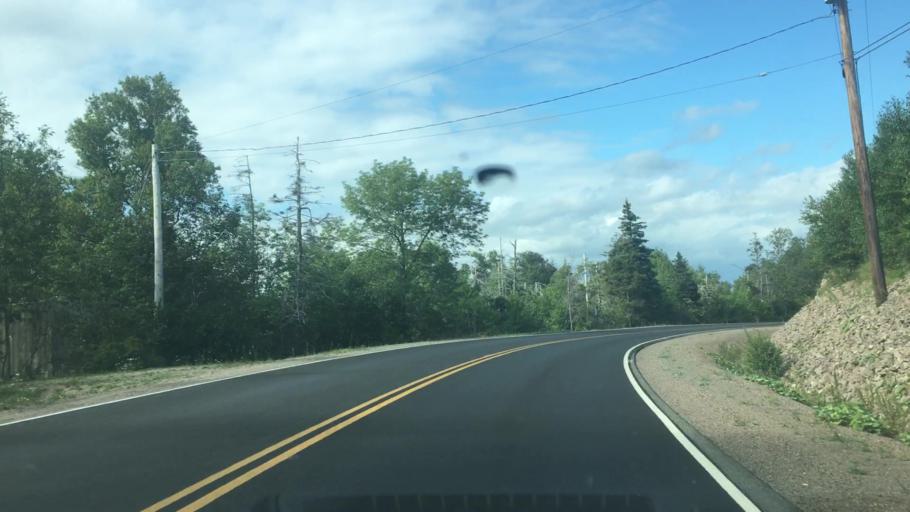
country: CA
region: Nova Scotia
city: Princeville
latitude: 45.7942
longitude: -60.7370
